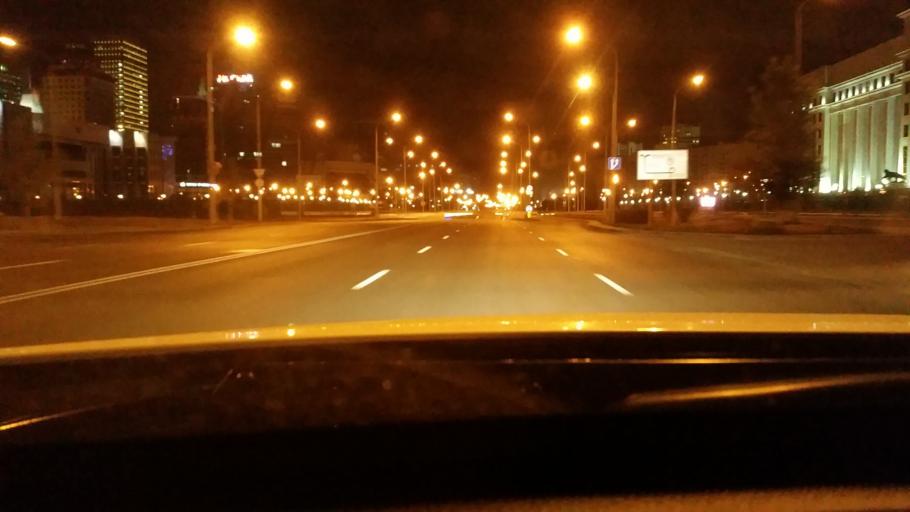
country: KZ
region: Astana Qalasy
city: Astana
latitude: 51.1186
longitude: 71.4353
